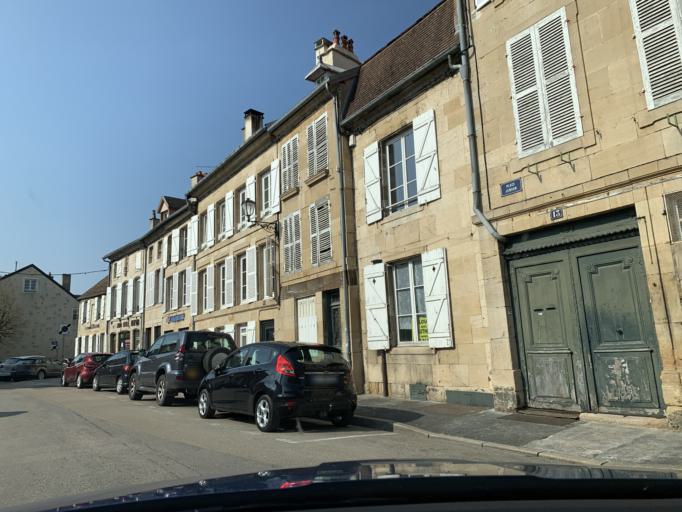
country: FR
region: Champagne-Ardenne
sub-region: Departement de la Haute-Marne
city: Langres
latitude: 47.8607
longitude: 5.3320
